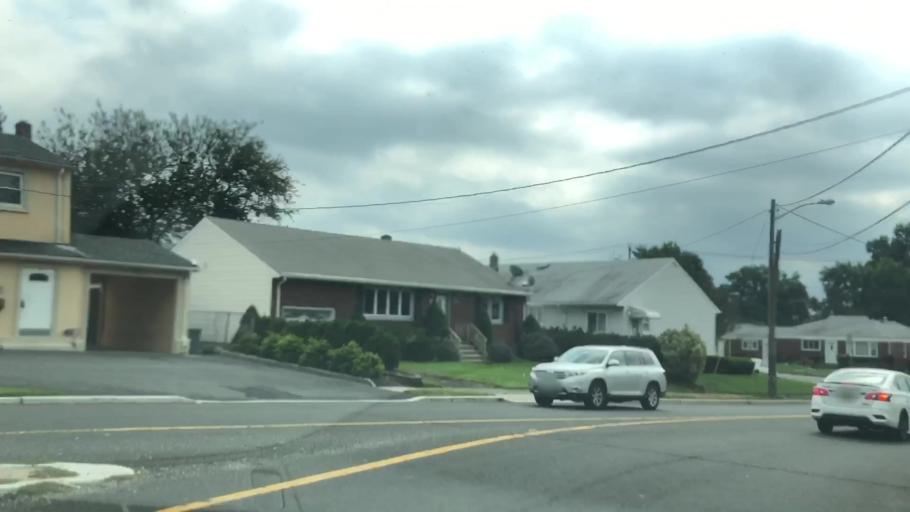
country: US
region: New Jersey
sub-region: Essex County
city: Nutley
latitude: 40.8338
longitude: -74.1481
